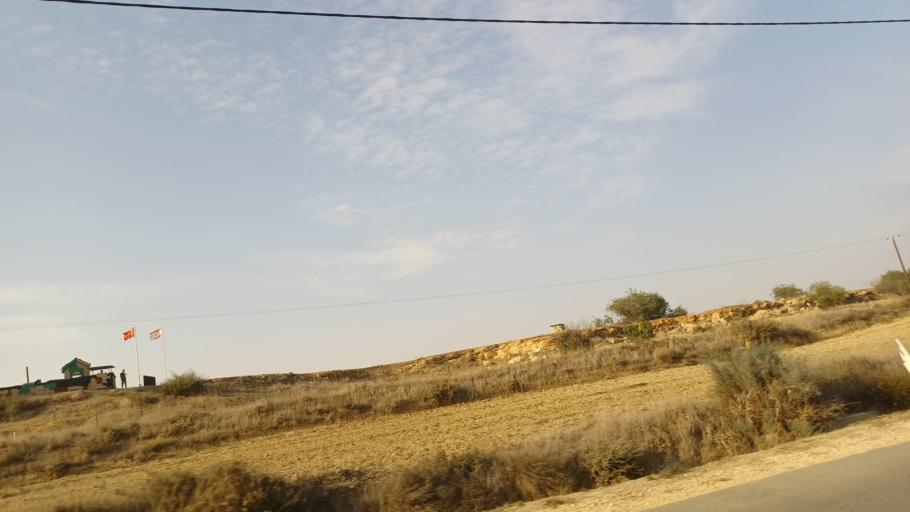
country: CY
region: Ammochostos
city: Acheritou
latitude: 35.0786
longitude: 33.8683
